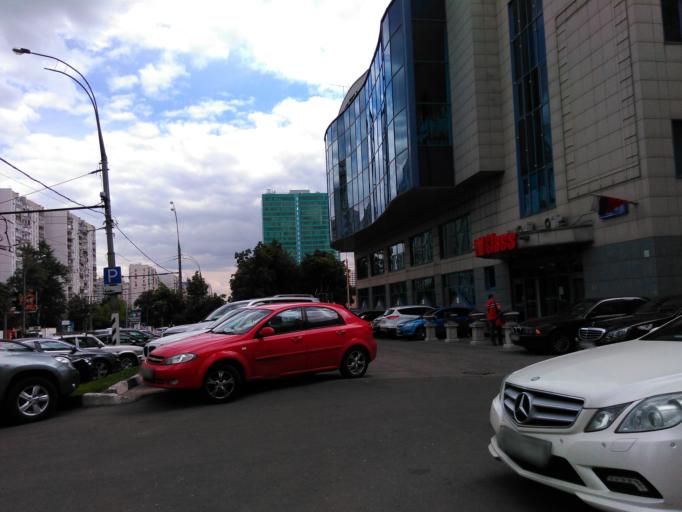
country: RU
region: Moskovskaya
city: Cheremushki
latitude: 55.6639
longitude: 37.5494
